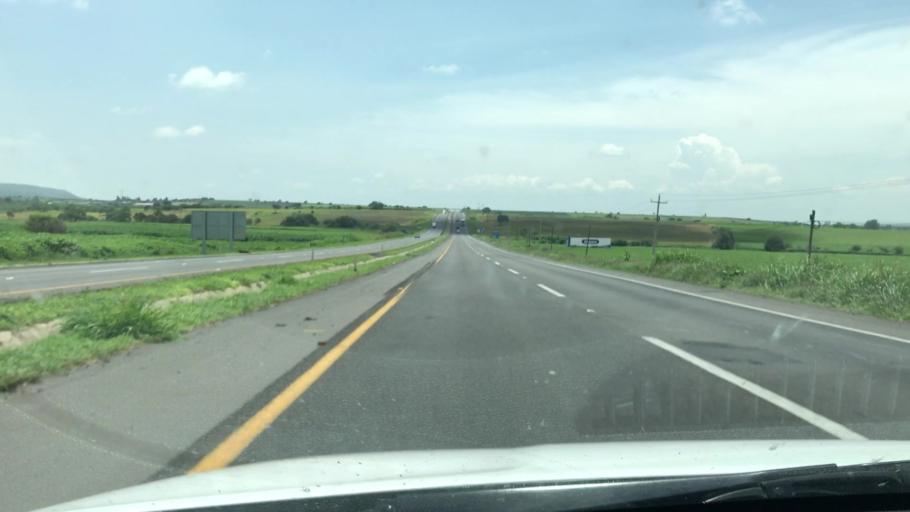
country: MX
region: Guanajuato
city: Penjamo
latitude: 20.3812
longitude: -101.8188
